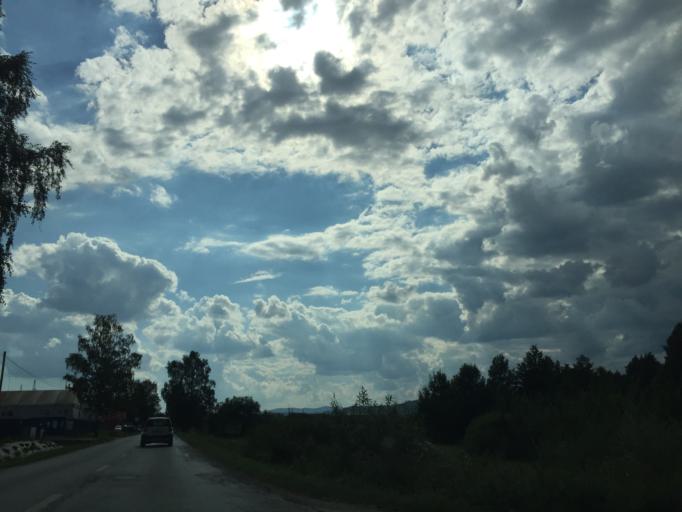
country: SK
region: Zilinsky
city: Namestovo
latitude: 49.3953
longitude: 19.4837
